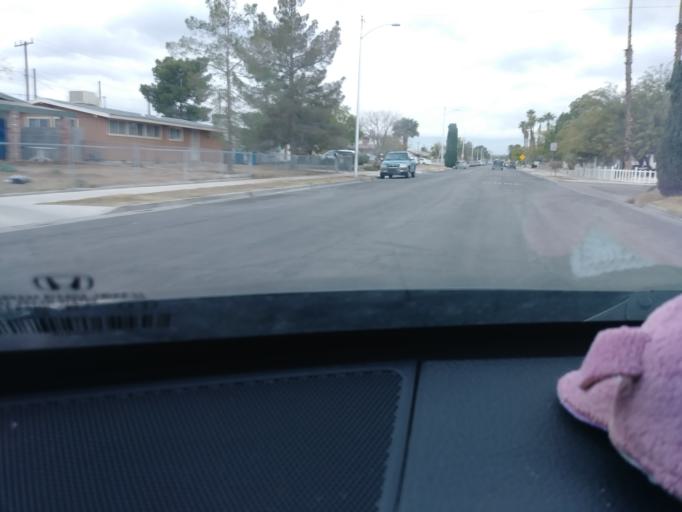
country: US
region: Nevada
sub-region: Clark County
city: Spring Valley
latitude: 36.1632
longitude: -115.2199
